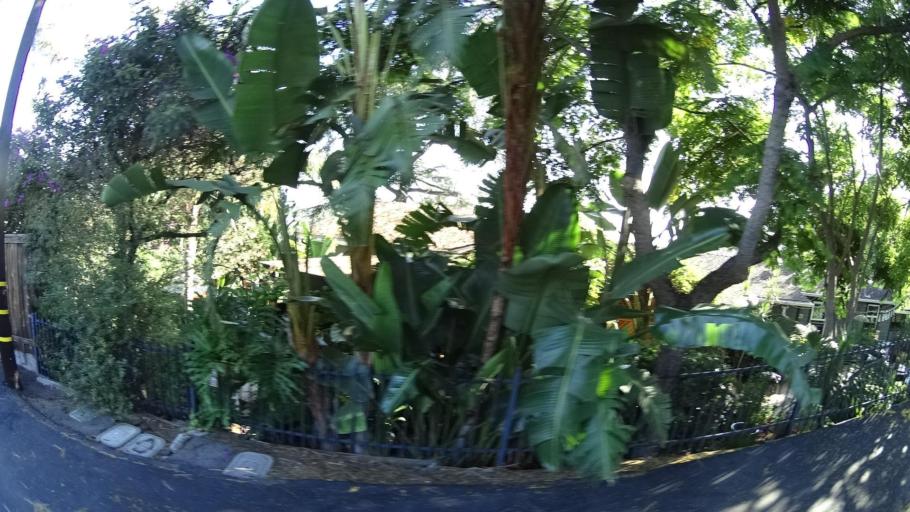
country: US
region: California
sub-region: San Diego County
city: Casa de Oro-Mount Helix
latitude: 32.7775
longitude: -116.9867
